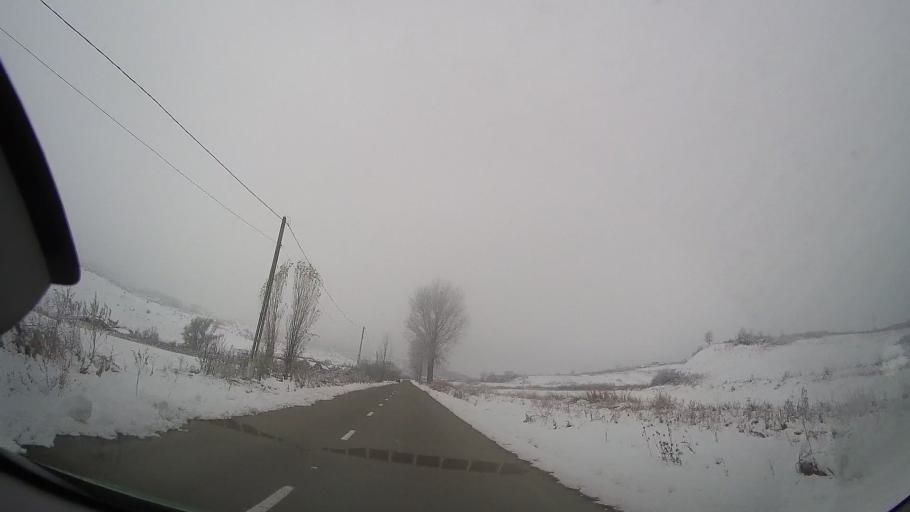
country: RO
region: Neamt
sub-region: Comuna Oniceni
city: Oniceni
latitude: 46.8006
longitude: 27.1234
